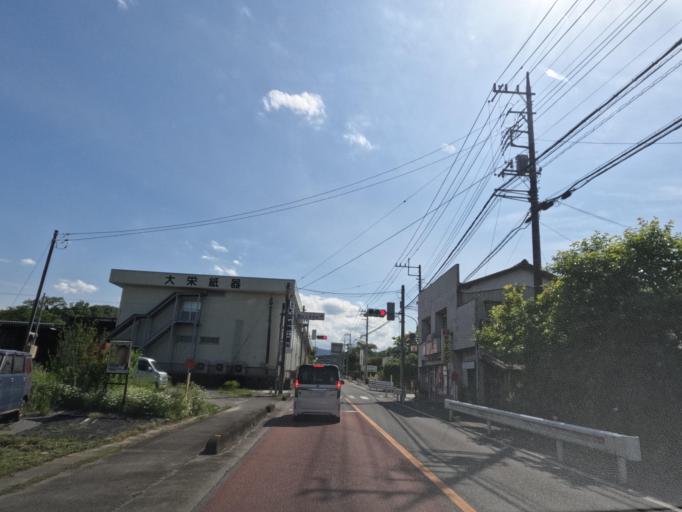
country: JP
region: Saitama
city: Ogawa
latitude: 36.0728
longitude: 139.2785
